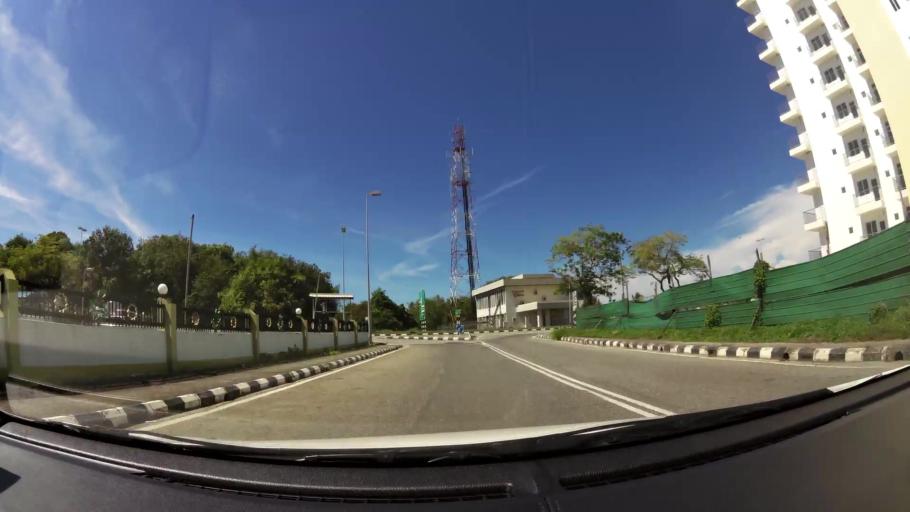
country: BN
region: Brunei and Muara
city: Bandar Seri Begawan
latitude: 5.0291
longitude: 115.0619
